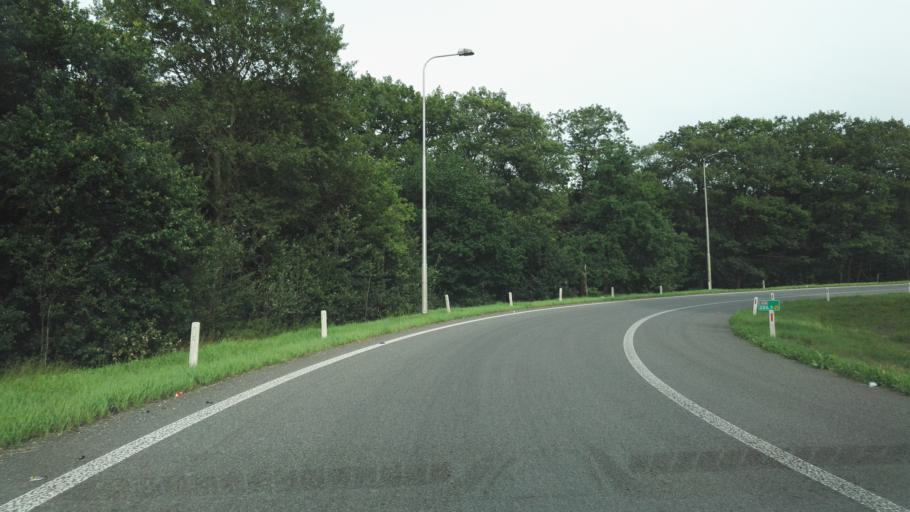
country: NL
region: Gelderland
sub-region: Gemeente Apeldoorn
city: Apeldoorn
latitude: 52.2092
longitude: 6.0232
